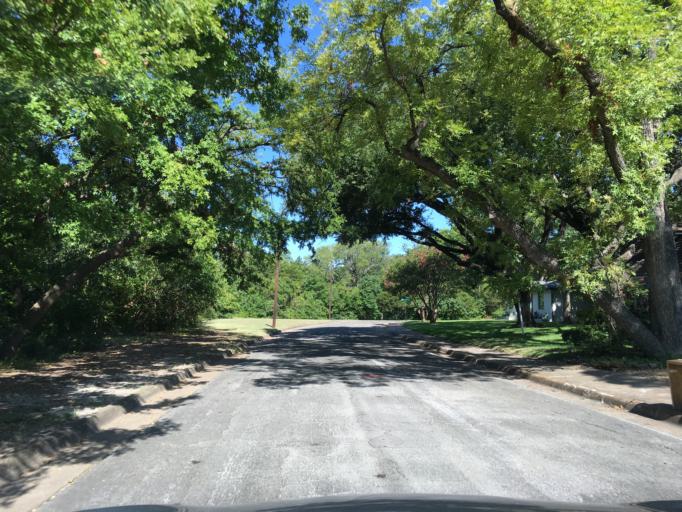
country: US
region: Texas
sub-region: Dallas County
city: Garland
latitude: 32.8564
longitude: -96.6995
